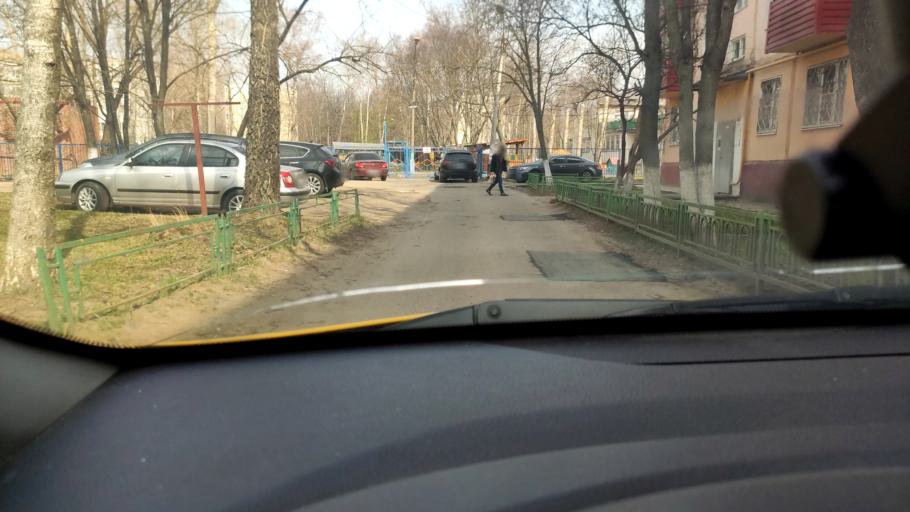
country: RU
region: Moskovskaya
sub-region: Chekhovskiy Rayon
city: Chekhov
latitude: 55.1531
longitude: 37.4714
